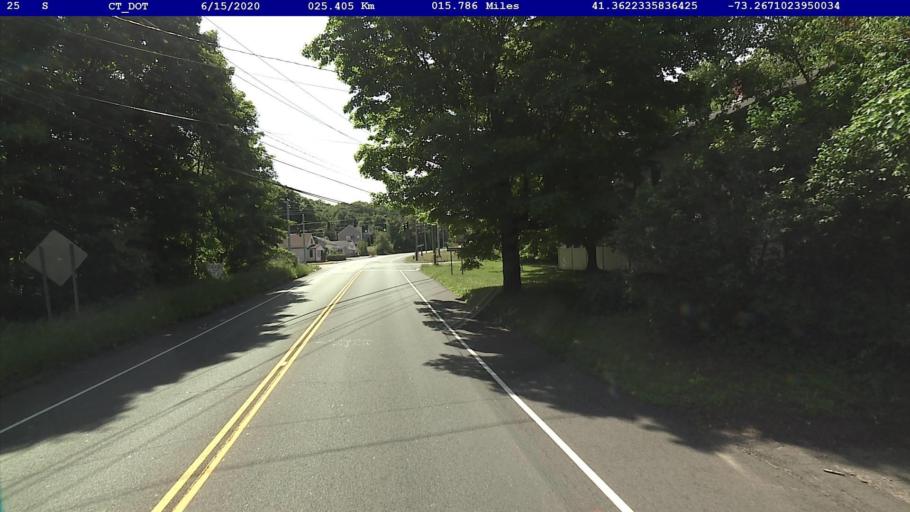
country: US
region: Connecticut
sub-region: Fairfield County
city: Newtown
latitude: 41.3622
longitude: -73.2672
